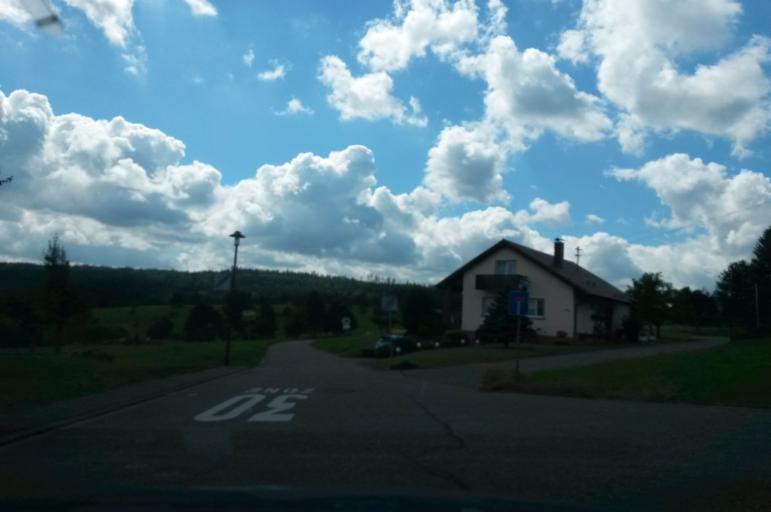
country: DE
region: Baden-Wuerttemberg
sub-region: Karlsruhe Region
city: Bad Herrenalb
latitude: 48.8426
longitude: 8.4523
